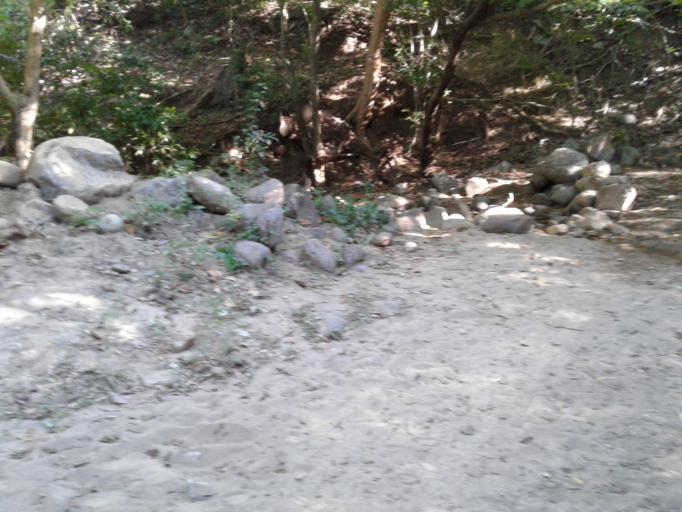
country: NI
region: Carazo
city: Santa Teresa
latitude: 11.6581
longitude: -86.1696
